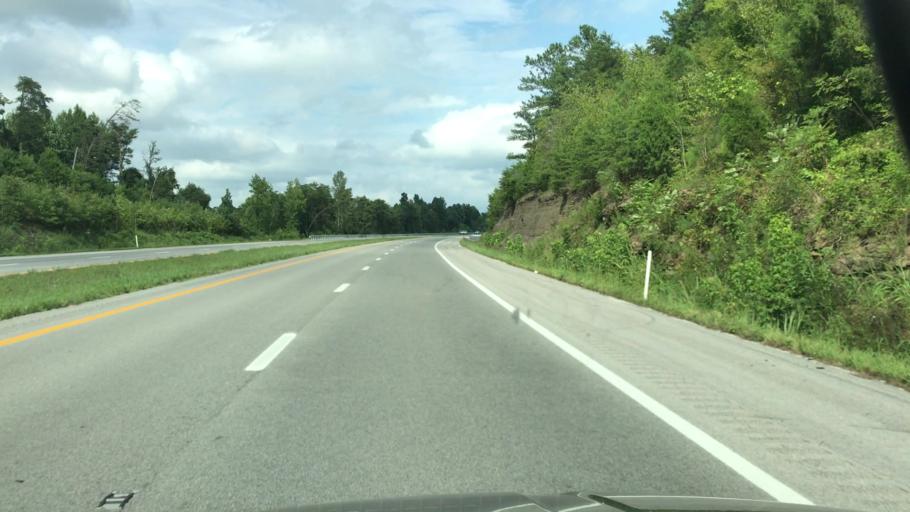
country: US
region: Kentucky
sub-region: Hopkins County
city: Dawson Springs
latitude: 37.1638
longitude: -87.7585
